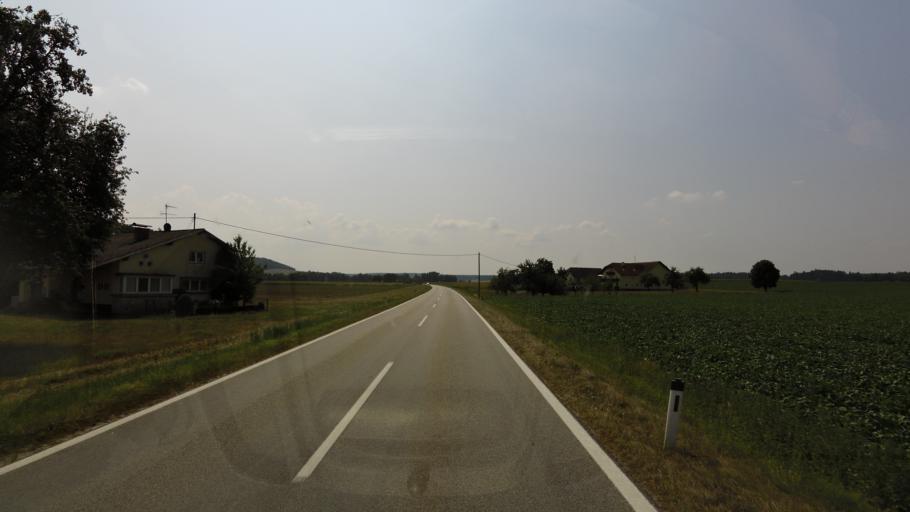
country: DE
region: Bavaria
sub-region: Lower Bavaria
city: Bad Fussing
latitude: 48.2729
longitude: 13.3291
